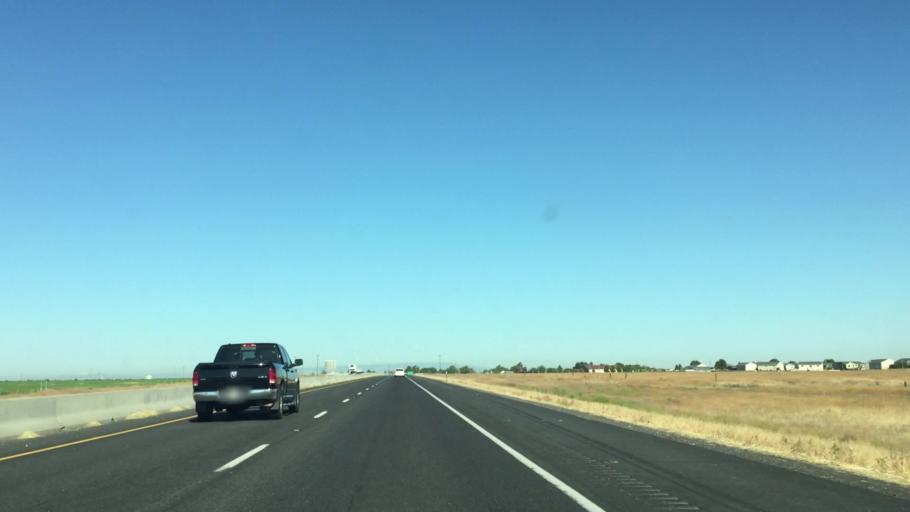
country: US
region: Washington
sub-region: Grant County
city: Moses Lake
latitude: 47.1015
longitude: -119.2635
